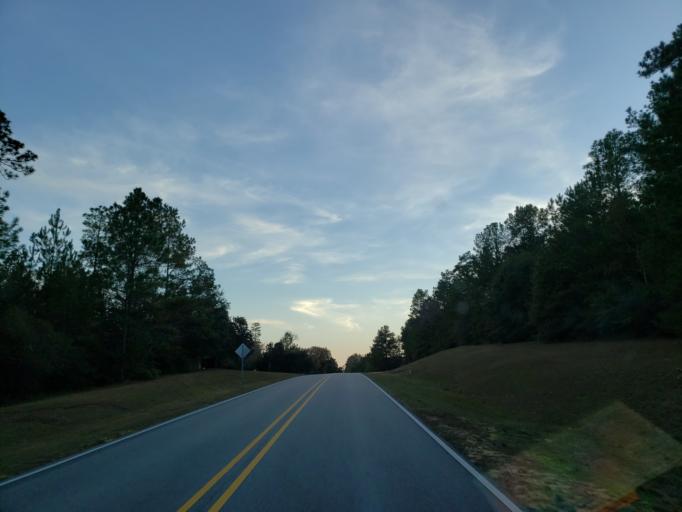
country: US
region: Mississippi
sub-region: Forrest County
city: Hattiesburg
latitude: 31.2589
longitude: -89.3141
